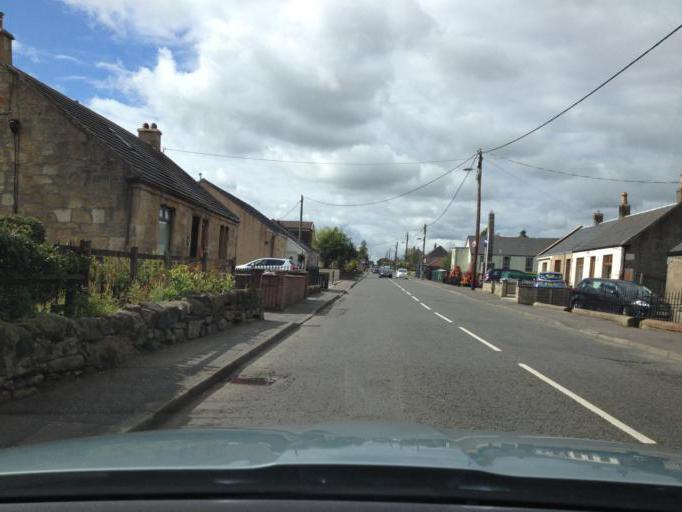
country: GB
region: Scotland
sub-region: Falkirk
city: Falkirk
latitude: 55.9716
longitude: -3.7664
